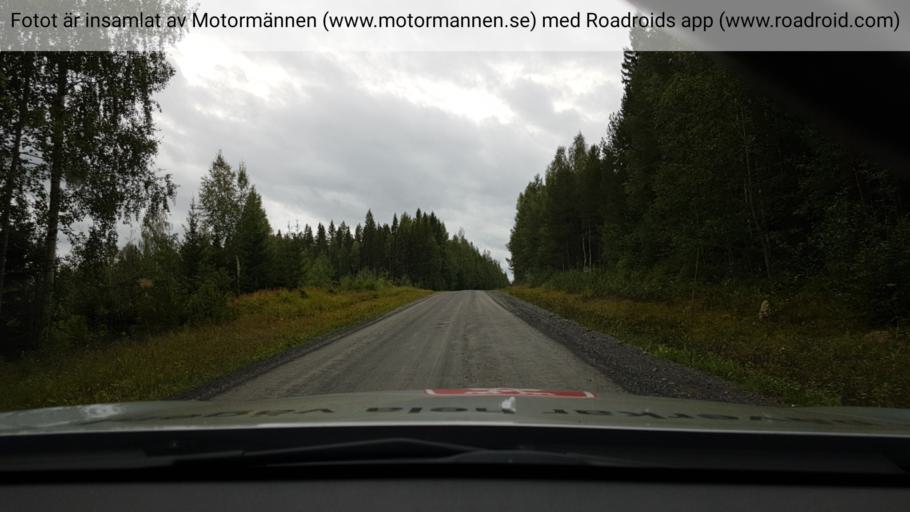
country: SE
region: Vaesterbotten
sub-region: Skelleftea Kommun
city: Forsbacka
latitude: 64.8327
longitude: 20.5018
